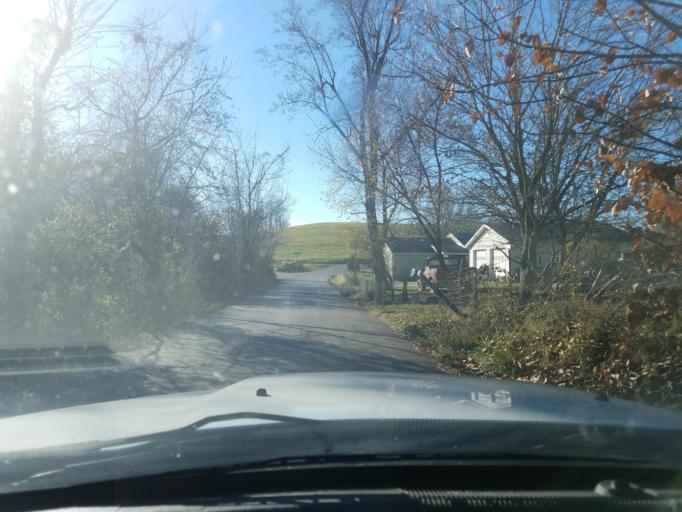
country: US
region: West Virginia
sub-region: Jackson County
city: Ripley
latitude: 38.7996
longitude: -81.9066
